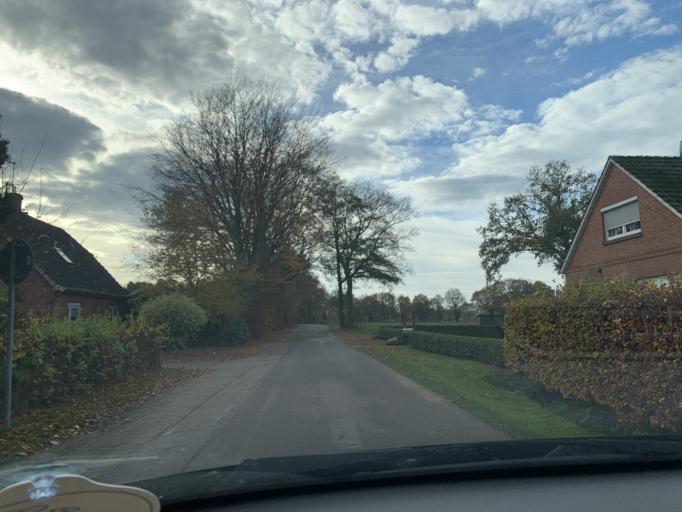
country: DE
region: Lower Saxony
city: Apen
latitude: 53.2236
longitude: 7.7864
